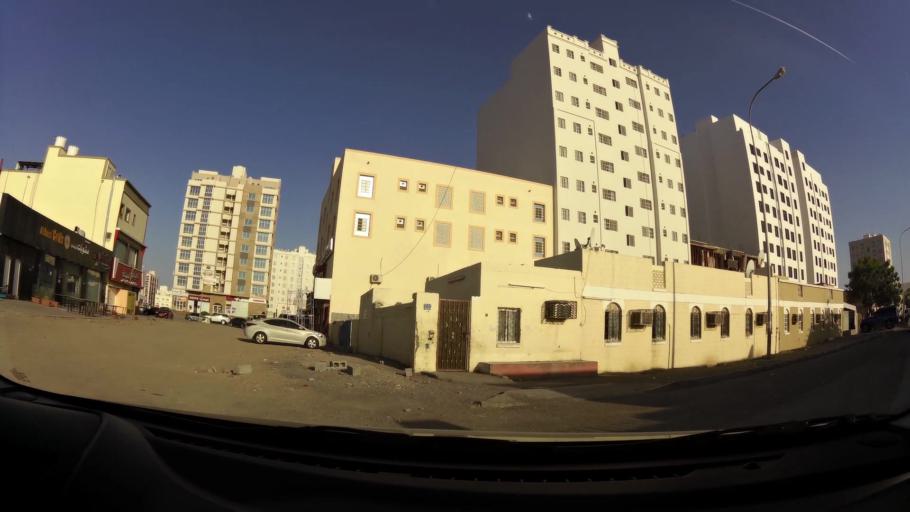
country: OM
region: Muhafazat Masqat
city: As Sib al Jadidah
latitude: 23.6274
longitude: 58.1947
